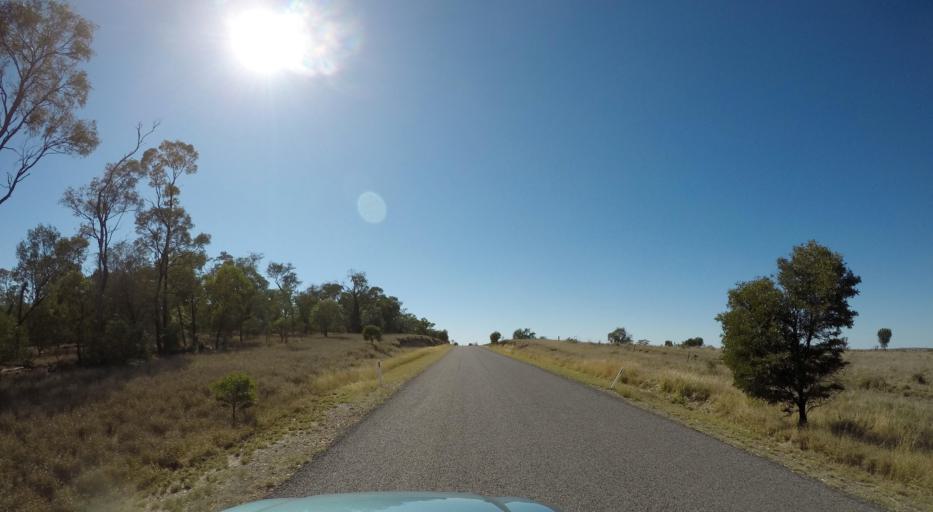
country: AU
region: Queensland
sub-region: Banana
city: Taroom
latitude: -25.7886
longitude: 149.6873
